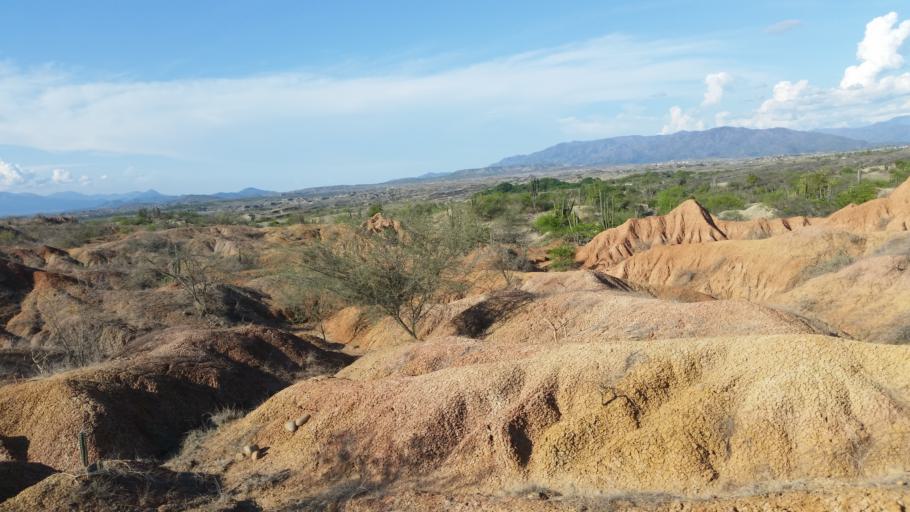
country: CO
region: Huila
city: Villavieja
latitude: 3.2286
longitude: -75.1515
